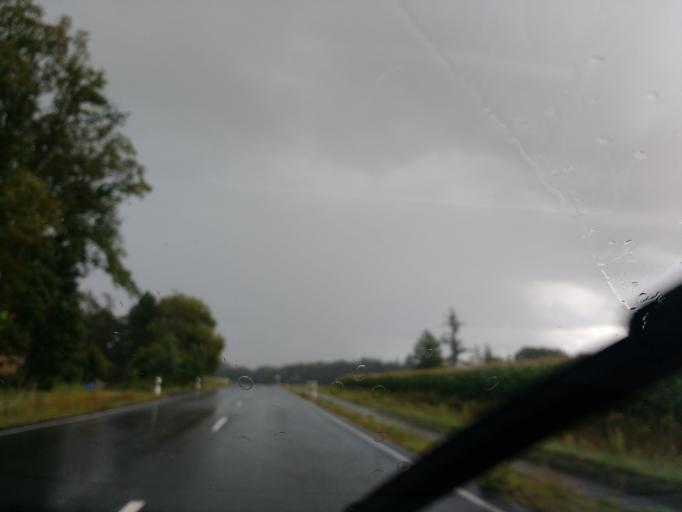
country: DE
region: North Rhine-Westphalia
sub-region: Regierungsbezirk Munster
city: Ladbergen
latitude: 52.1295
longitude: 7.8023
